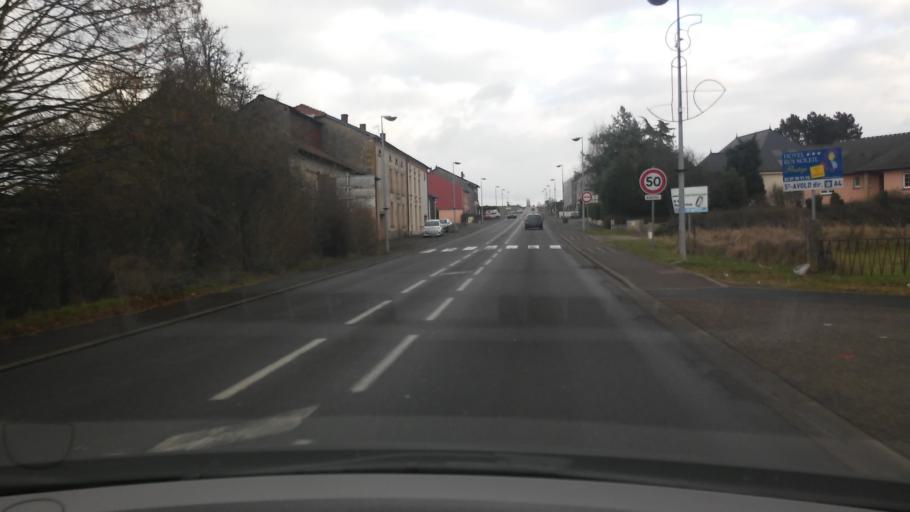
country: FR
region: Lorraine
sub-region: Departement de la Moselle
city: Longeville-les-Saint-Avold
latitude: 49.1168
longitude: 6.6485
